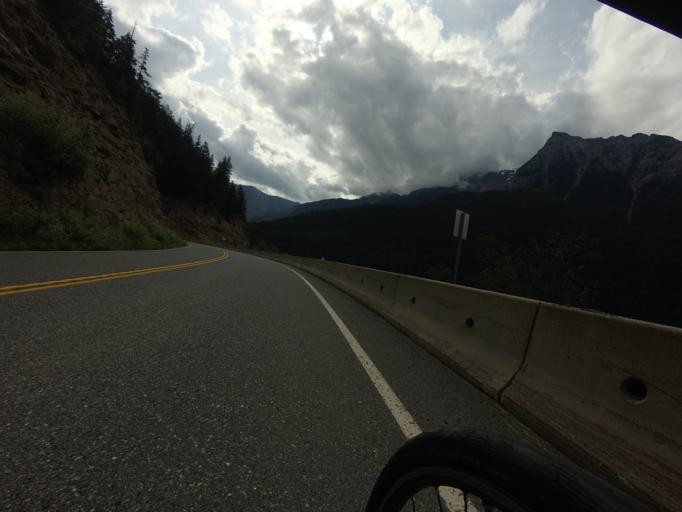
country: CA
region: British Columbia
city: Lillooet
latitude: 50.6422
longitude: -122.0300
